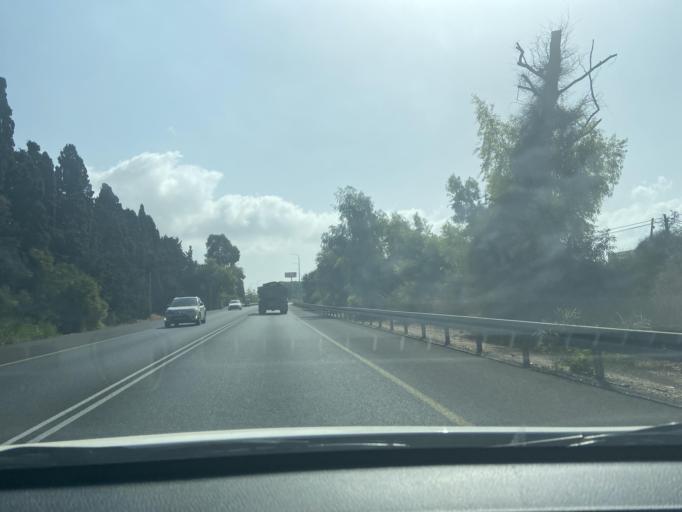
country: IL
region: Northern District
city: Nahariya
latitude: 33.0369
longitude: 35.1052
